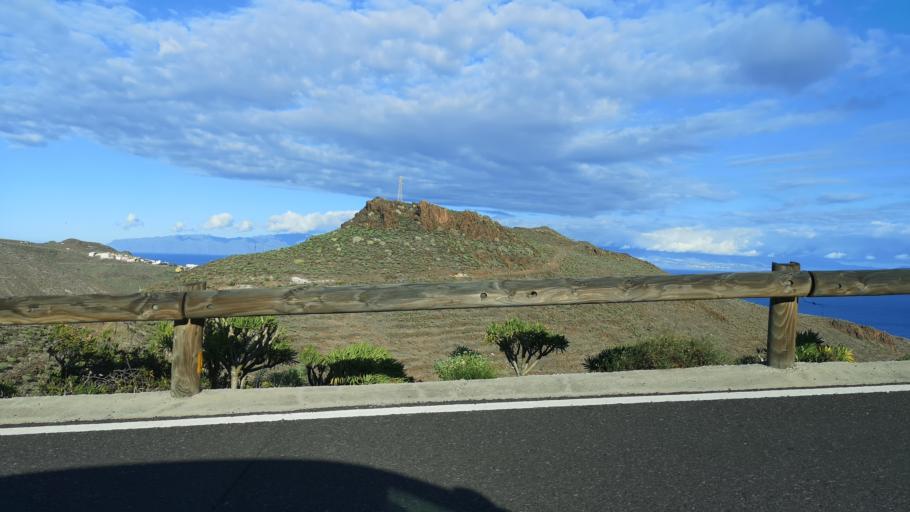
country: ES
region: Canary Islands
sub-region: Provincia de Santa Cruz de Tenerife
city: San Sebastian de la Gomera
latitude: 28.0820
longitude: -17.1271
